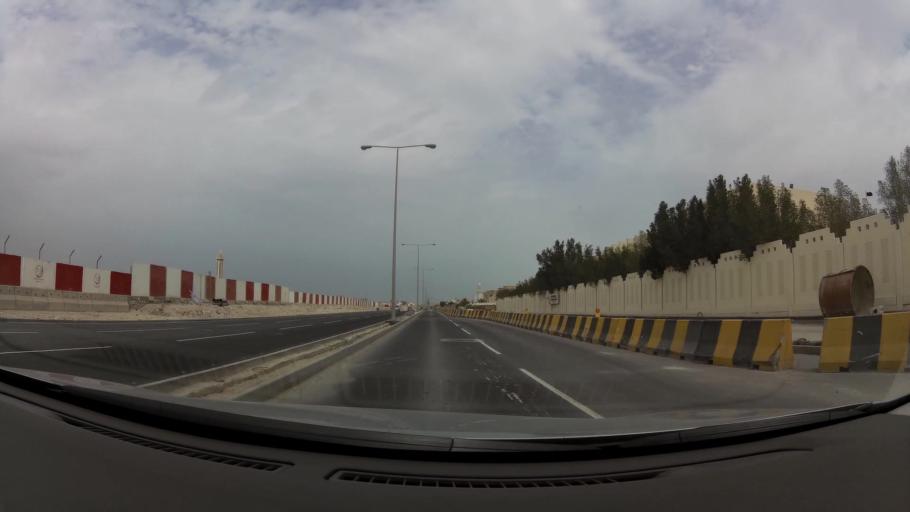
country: QA
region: Baladiyat ar Rayyan
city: Ar Rayyan
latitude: 25.3554
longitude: 51.4674
